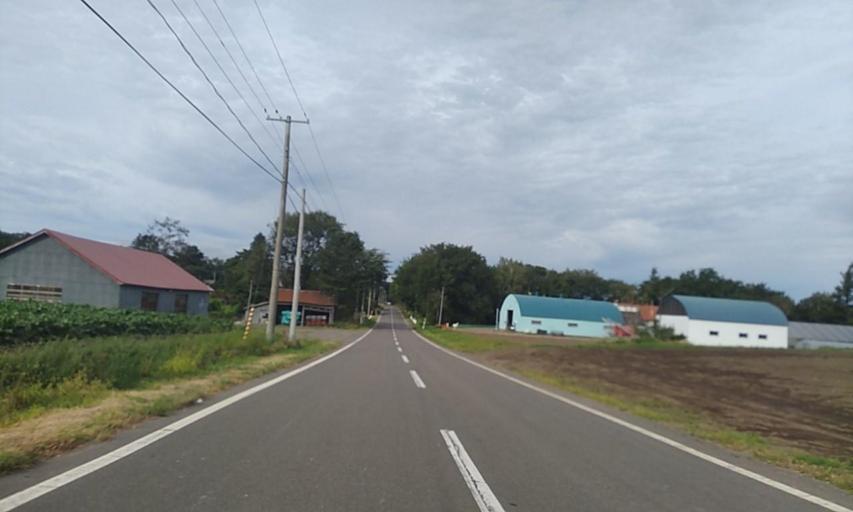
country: JP
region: Hokkaido
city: Abashiri
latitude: 43.7959
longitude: 144.5576
